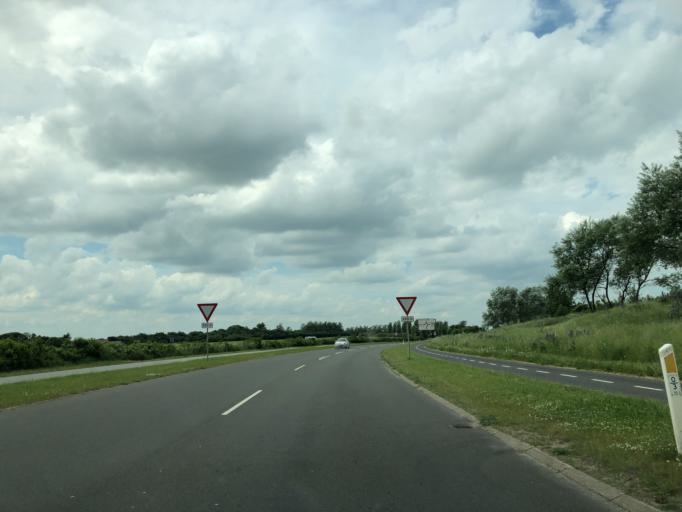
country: DK
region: Central Jutland
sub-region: Struer Kommune
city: Struer
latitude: 56.4734
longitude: 8.5911
